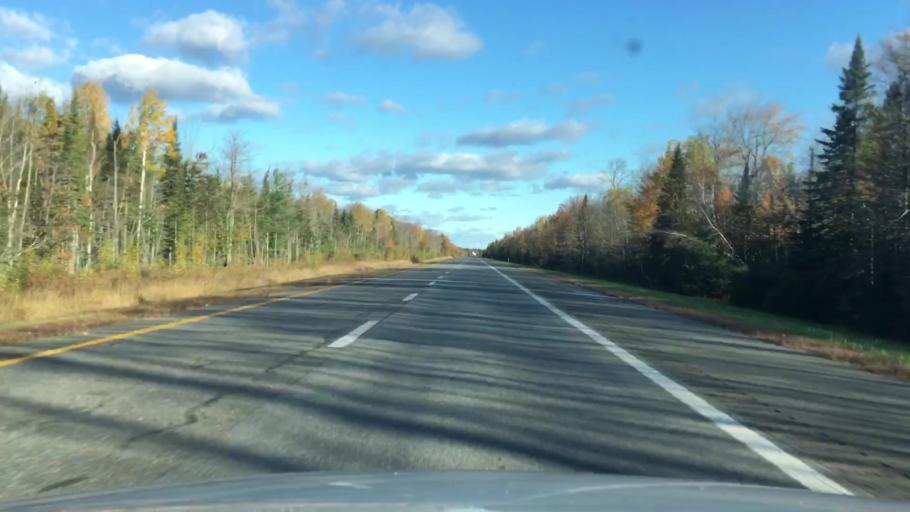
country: US
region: Maine
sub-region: Penobscot County
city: Greenbush
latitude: 45.0804
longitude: -68.6921
